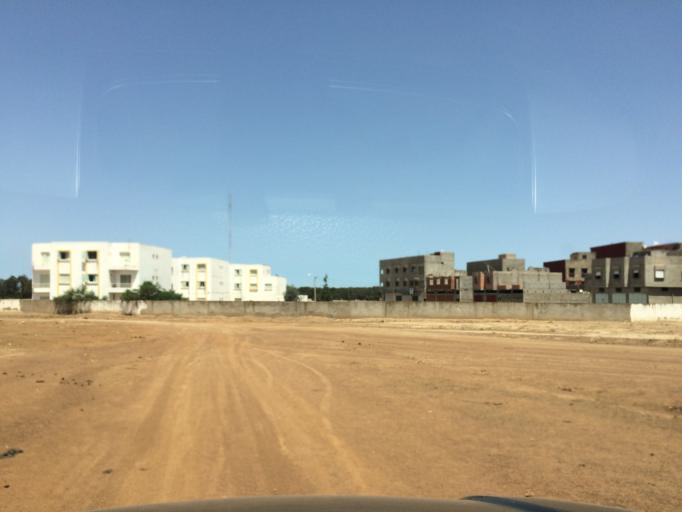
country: MA
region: Chaouia-Ouardigha
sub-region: Benslimane
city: Mellila
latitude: 33.5644
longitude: -6.8993
